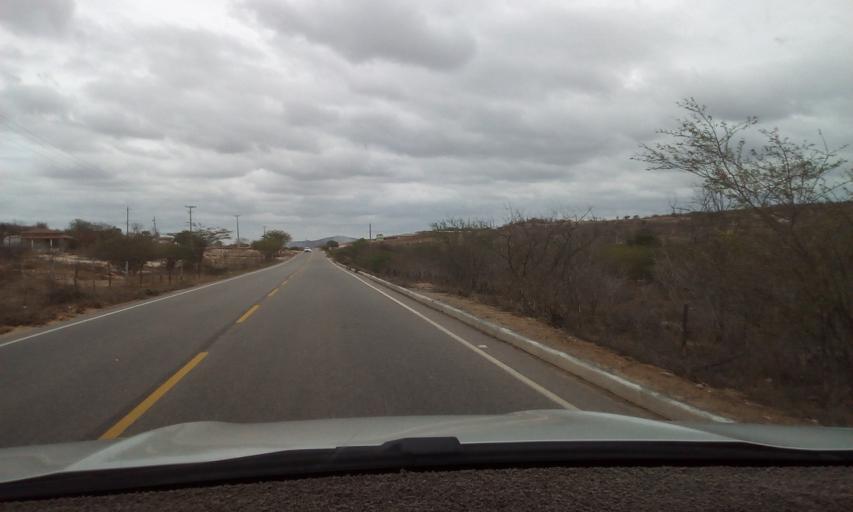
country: BR
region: Paraiba
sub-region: Picui
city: Picui
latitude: -6.5519
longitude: -36.2961
